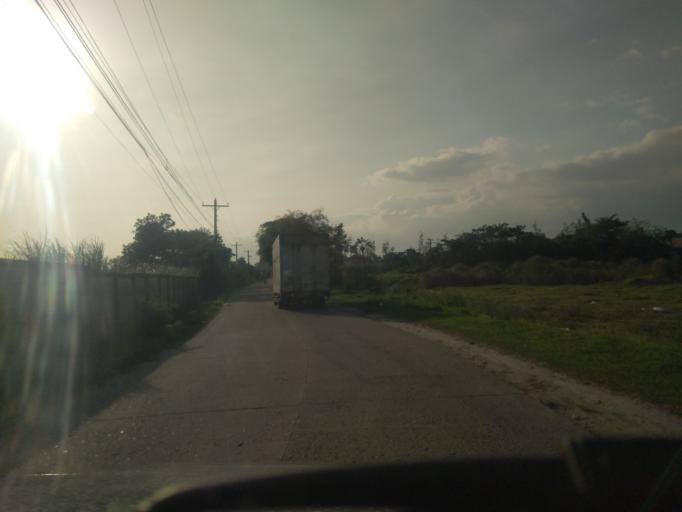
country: PH
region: Central Luzon
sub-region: Province of Pampanga
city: Malino
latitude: 15.1108
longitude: 120.6670
